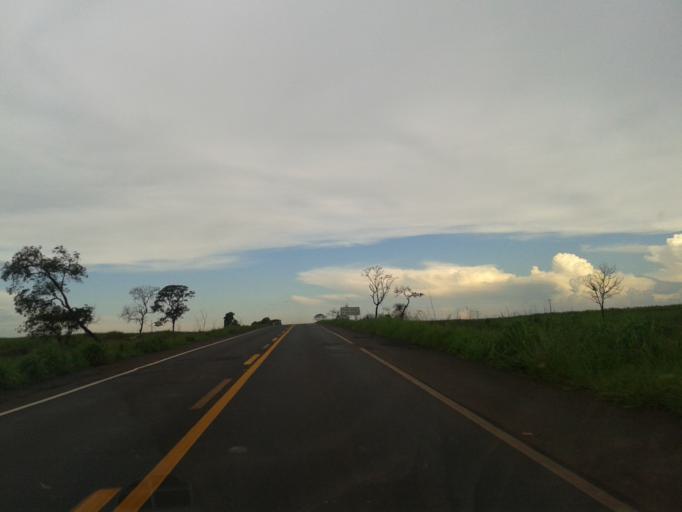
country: BR
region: Minas Gerais
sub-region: Santa Vitoria
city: Santa Vitoria
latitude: -18.8956
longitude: -50.1768
